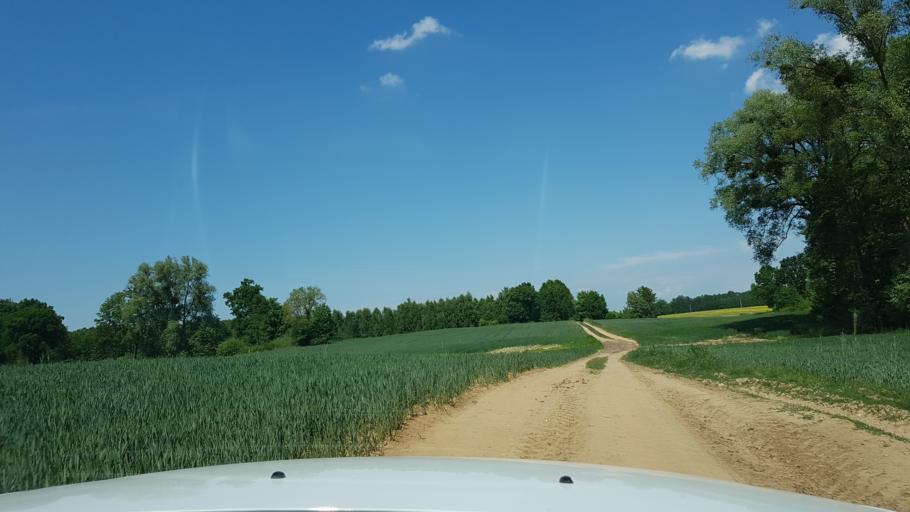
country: PL
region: West Pomeranian Voivodeship
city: Trzcinsko Zdroj
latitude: 52.9353
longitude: 14.5784
